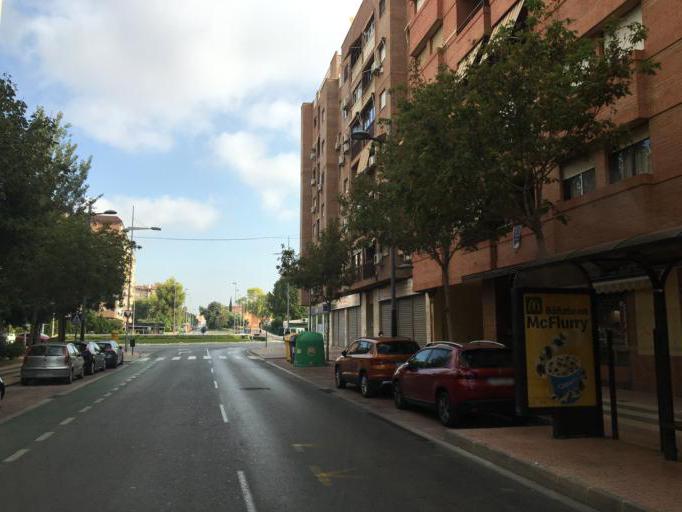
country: ES
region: Murcia
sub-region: Murcia
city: Cartagena
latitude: 37.6147
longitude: -0.9891
